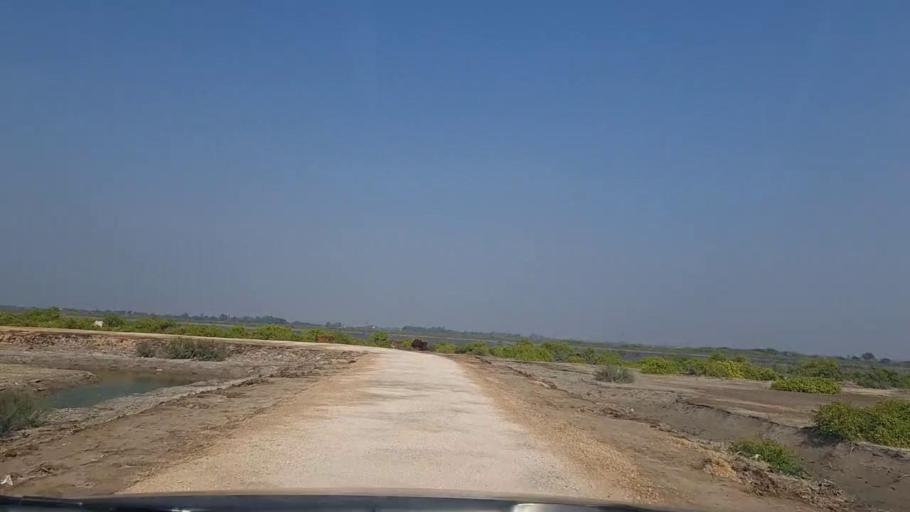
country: PK
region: Sindh
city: Mirpur Sakro
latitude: 24.5783
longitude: 67.7576
